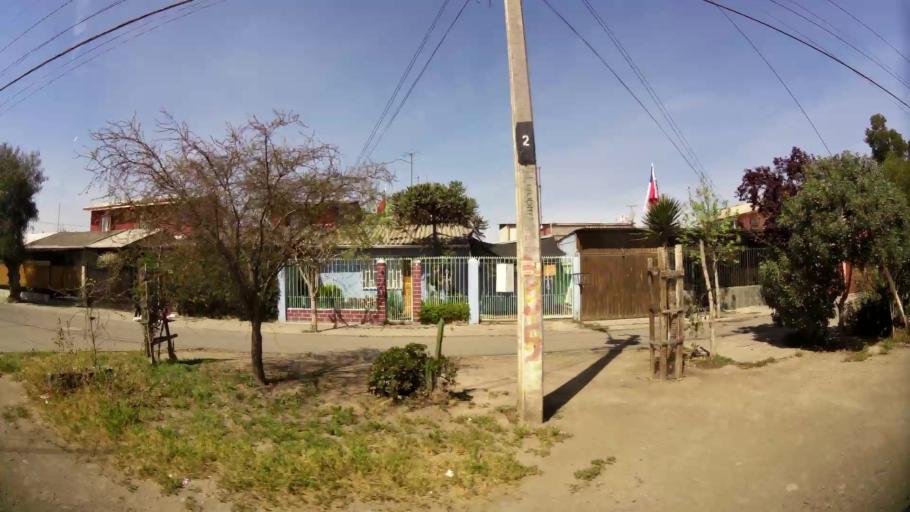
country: CL
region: Santiago Metropolitan
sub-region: Provincia de Maipo
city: San Bernardo
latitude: -33.5259
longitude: -70.6983
